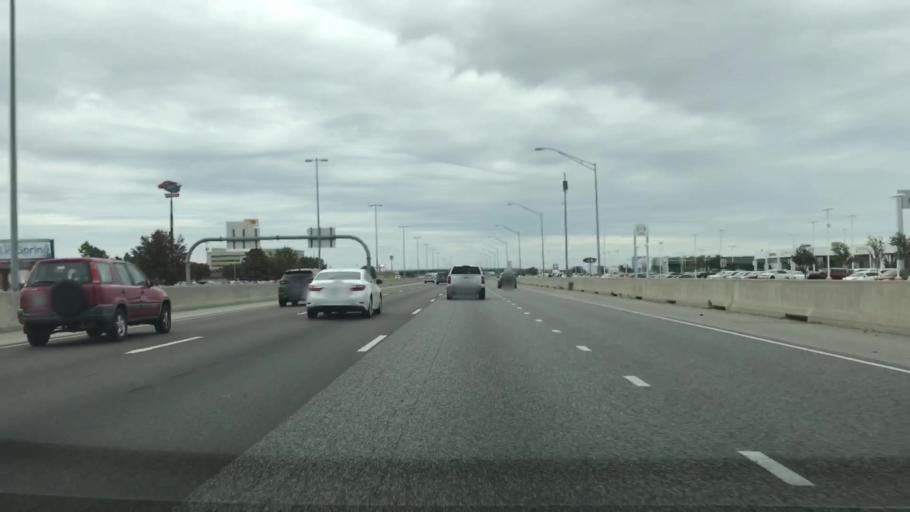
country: US
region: Oklahoma
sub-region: Cleveland County
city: Norman
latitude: 35.2261
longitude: -97.4854
